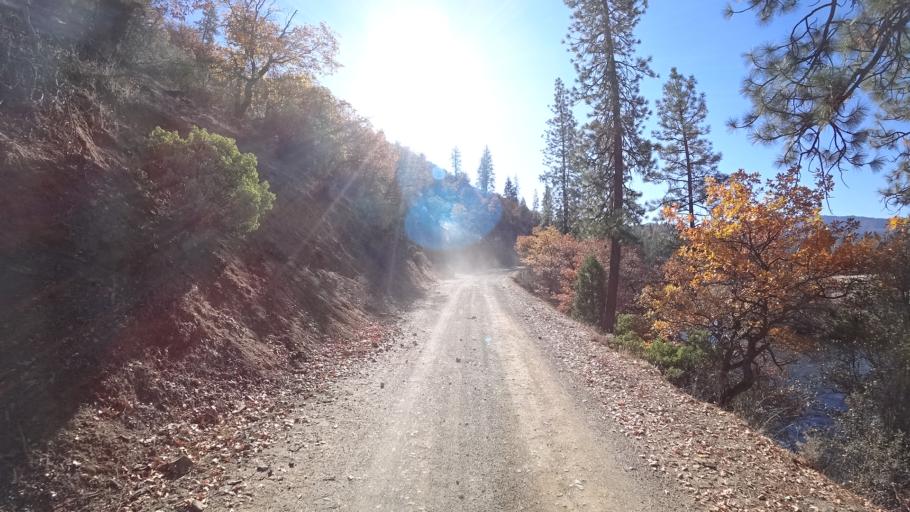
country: US
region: California
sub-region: Siskiyou County
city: Yreka
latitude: 41.8398
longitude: -122.8357
